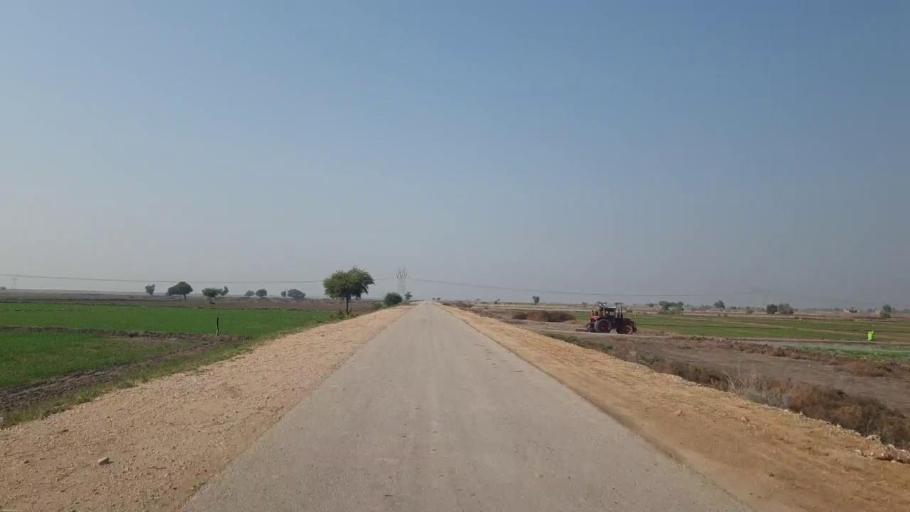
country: PK
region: Sindh
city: Sehwan
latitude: 26.4187
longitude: 67.8178
